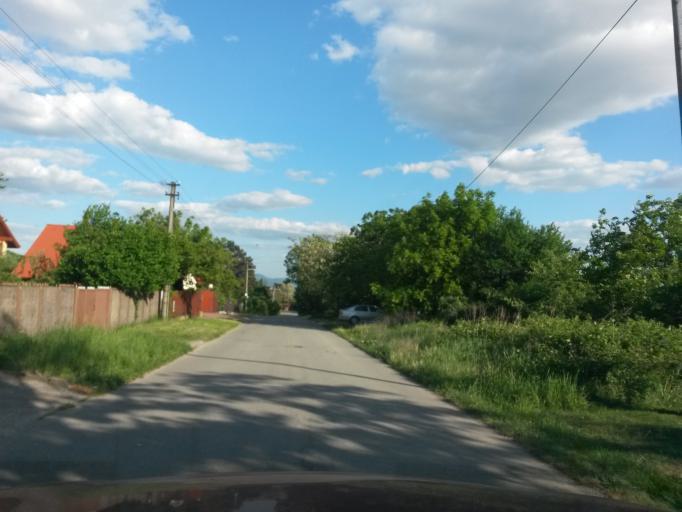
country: SK
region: Kosicky
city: Kosice
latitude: 48.6860
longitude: 21.2094
